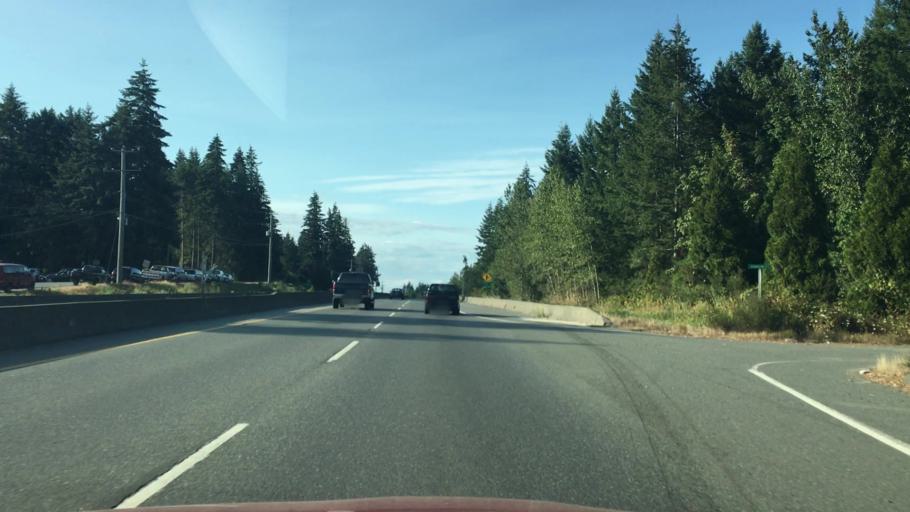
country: CA
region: British Columbia
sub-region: Cowichan Valley Regional District
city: Ladysmith
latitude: 48.9546
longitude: -123.7785
